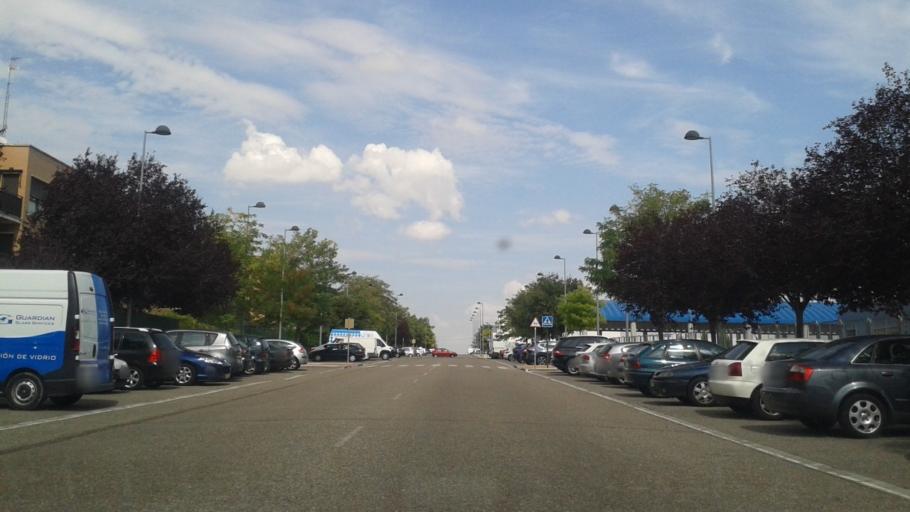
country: ES
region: Castille and Leon
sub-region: Provincia de Valladolid
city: Arroyo
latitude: 41.6258
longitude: -4.7766
